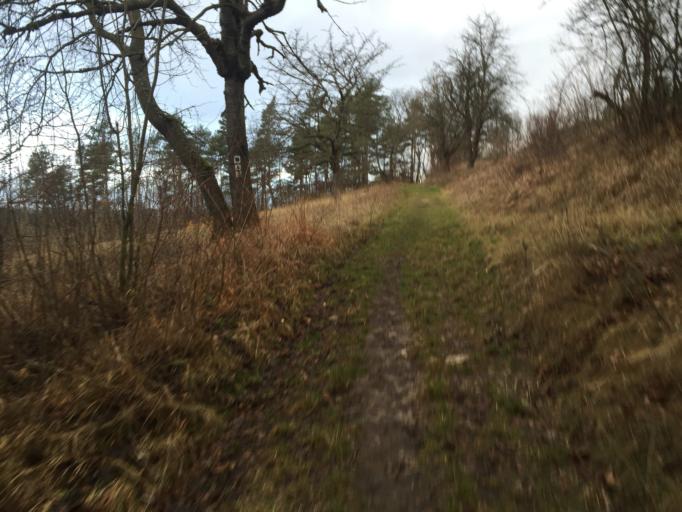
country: DE
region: Thuringia
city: Bad Blankenburg
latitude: 50.6978
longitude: 11.2563
